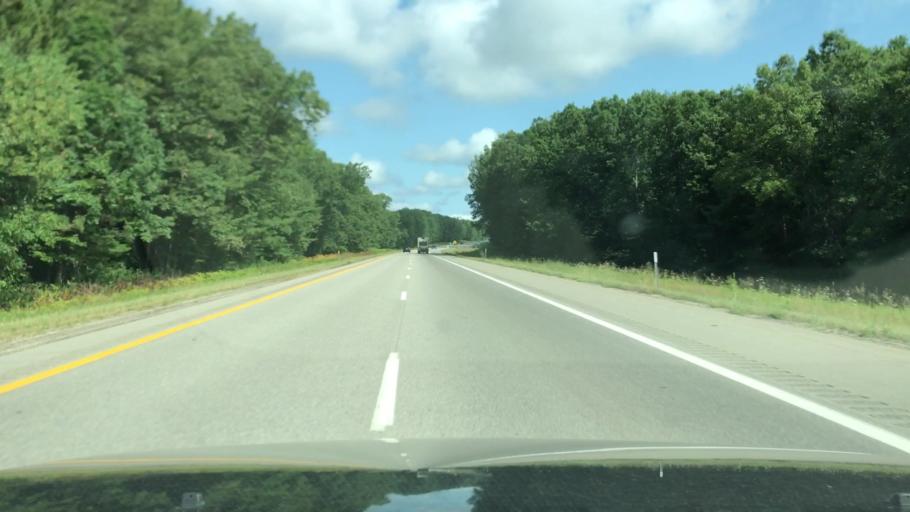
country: US
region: Michigan
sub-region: Montcalm County
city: Howard City
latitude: 43.4902
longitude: -85.4840
